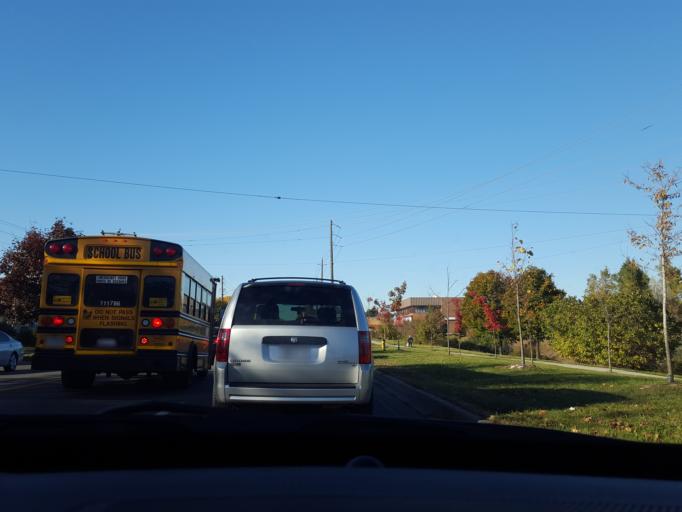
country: CA
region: Ontario
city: Scarborough
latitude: 43.7955
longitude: -79.2720
